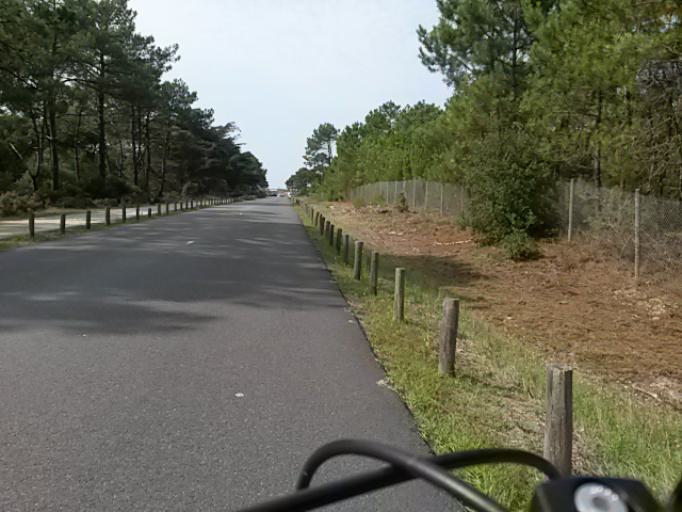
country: FR
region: Pays de la Loire
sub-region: Departement de la Loire-Atlantique
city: Le Croisic
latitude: 47.3163
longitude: -2.4984
